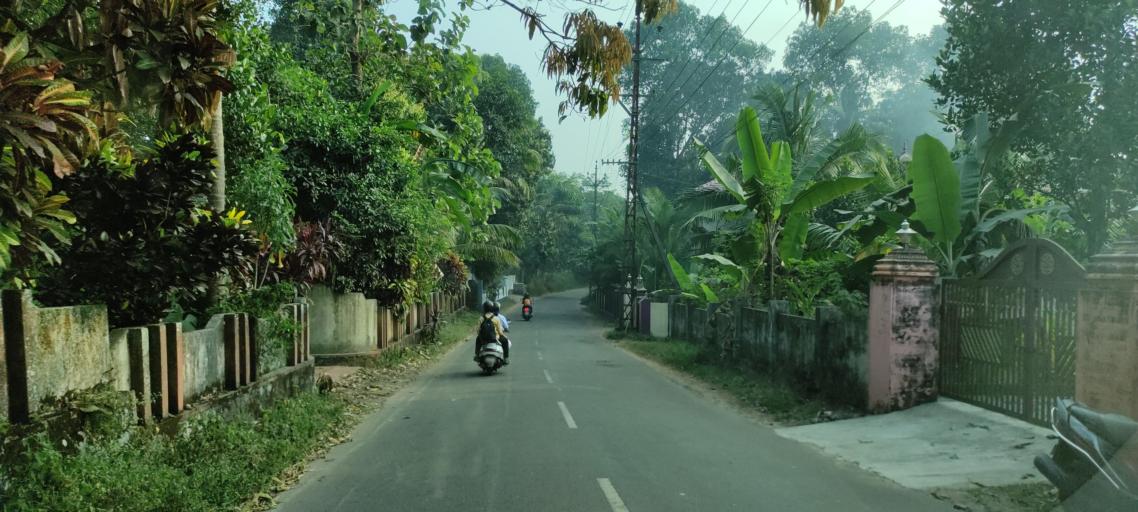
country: IN
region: Kerala
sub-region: Kottayam
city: Vaikam
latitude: 9.7325
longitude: 76.4786
